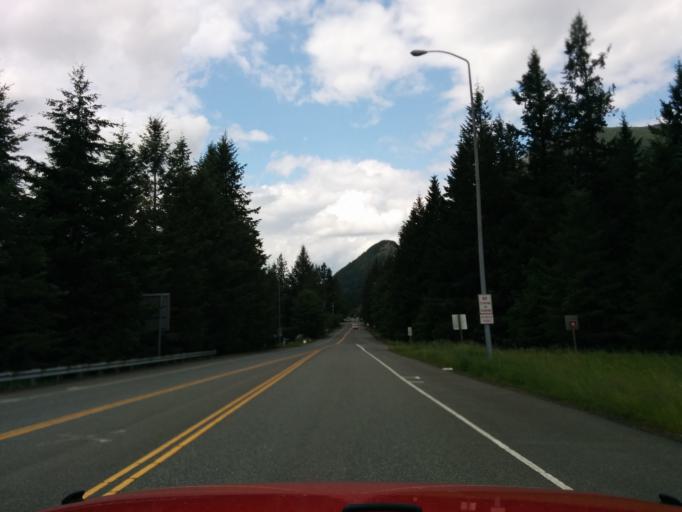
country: US
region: Washington
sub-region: King County
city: Riverbend
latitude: 47.4743
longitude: -121.7584
